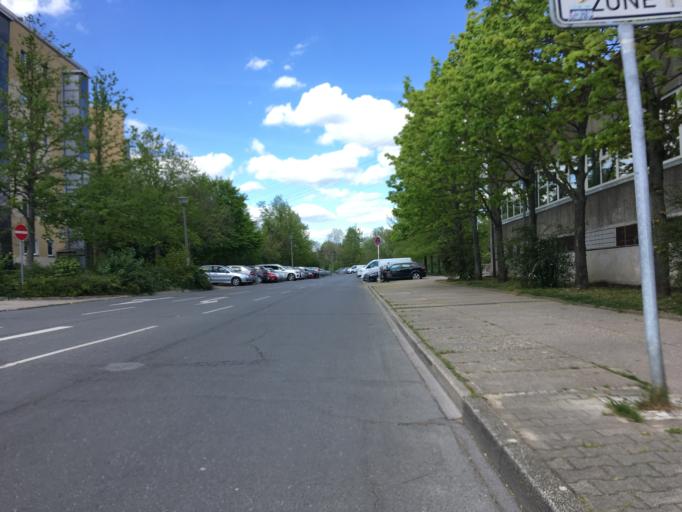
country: DE
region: Berlin
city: Hellersdorf
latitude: 52.5322
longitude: 13.6157
